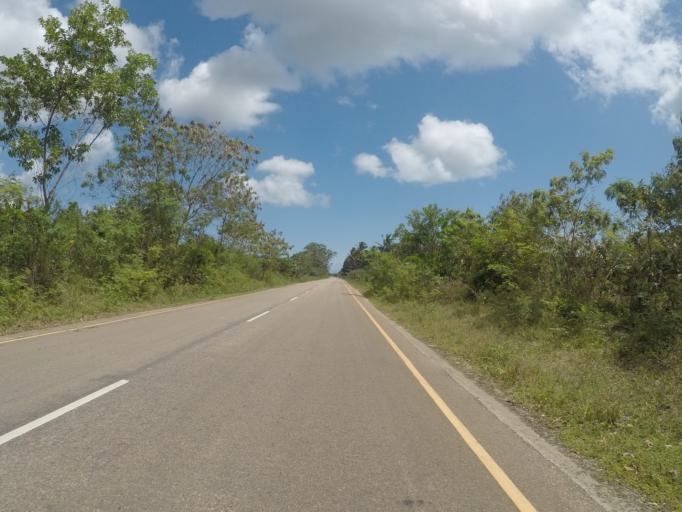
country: TZ
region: Zanzibar Central/South
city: Koani
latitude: -6.2379
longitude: 39.3585
